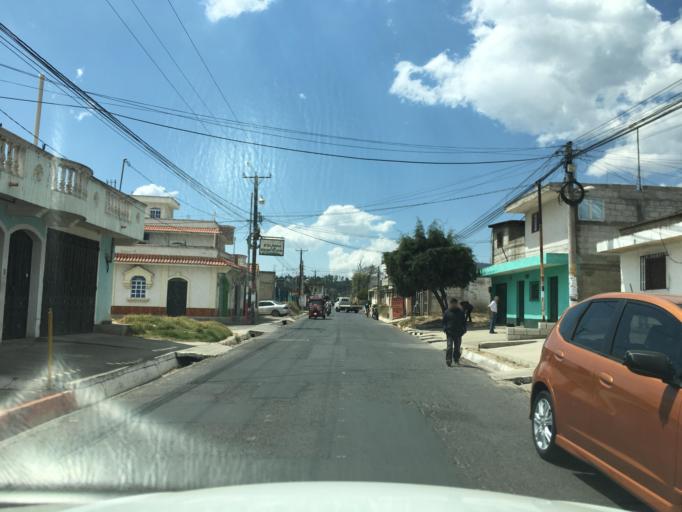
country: GT
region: Totonicapan
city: San Cristobal Totonicapan
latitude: 14.9093
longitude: -91.4513
